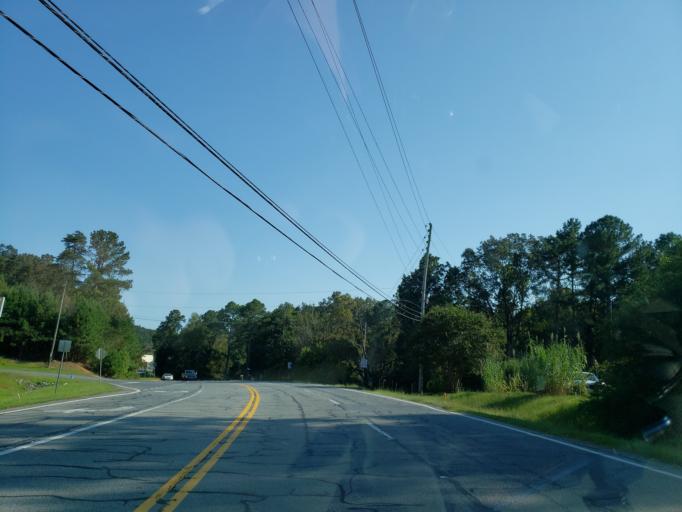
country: US
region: Georgia
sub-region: Whitfield County
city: Varnell
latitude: 34.8981
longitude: -84.9767
